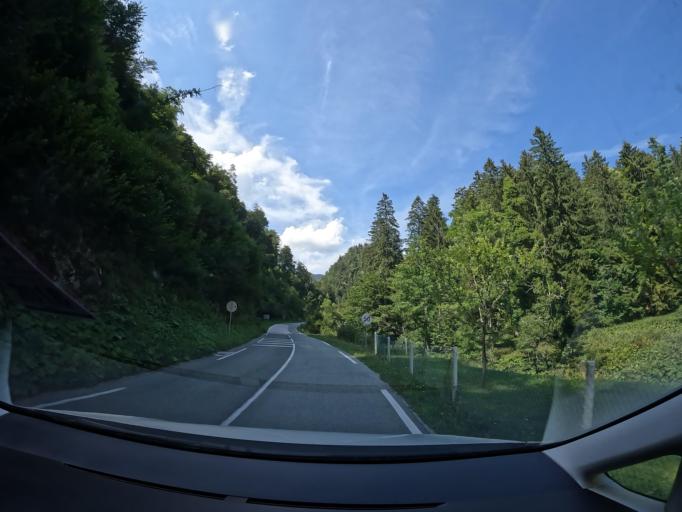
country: SI
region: Kranj
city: Golnik
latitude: 46.3847
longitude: 14.3756
